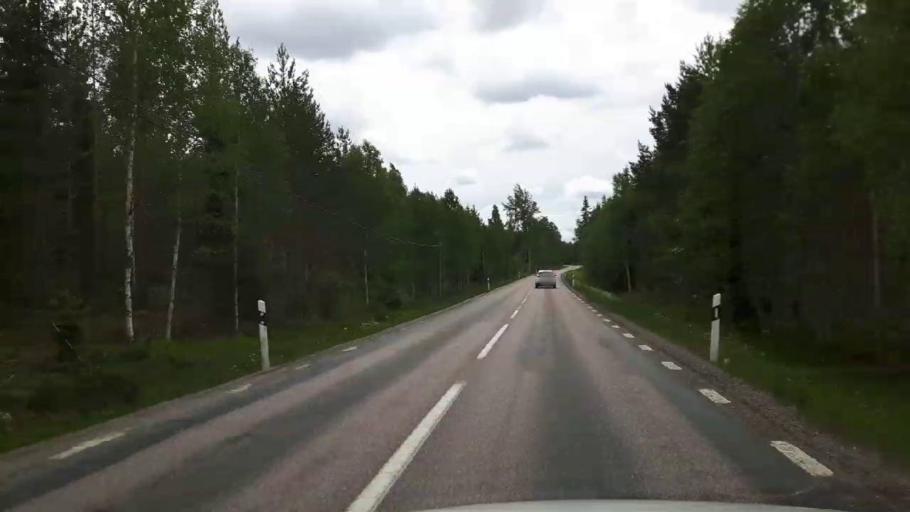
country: SE
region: Vaestmanland
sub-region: Norbergs Kommun
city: Norberg
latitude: 60.1167
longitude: 15.9202
